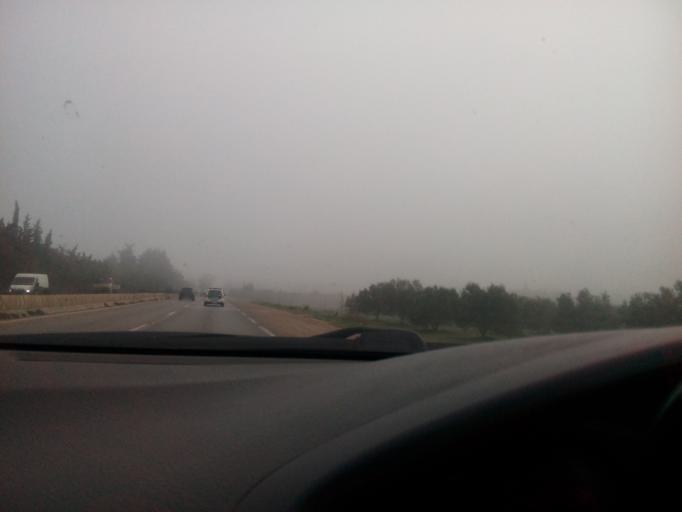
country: DZ
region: Oran
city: Bou Tlelis
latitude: 35.5836
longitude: -0.8213
